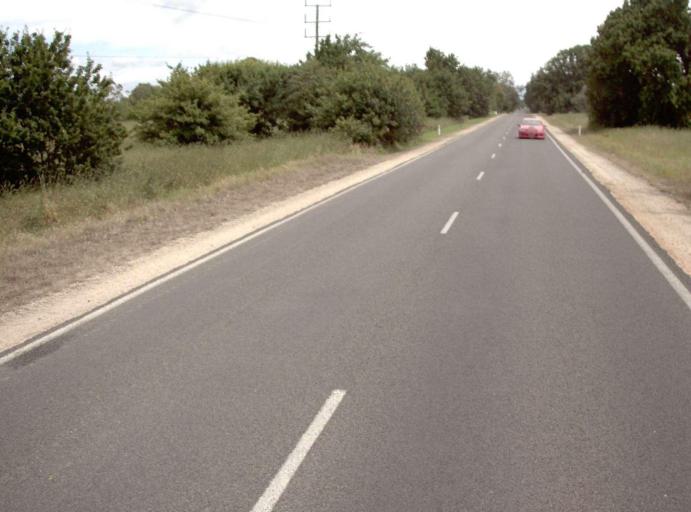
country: AU
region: Victoria
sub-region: Wellington
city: Sale
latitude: -38.0068
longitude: 147.0050
